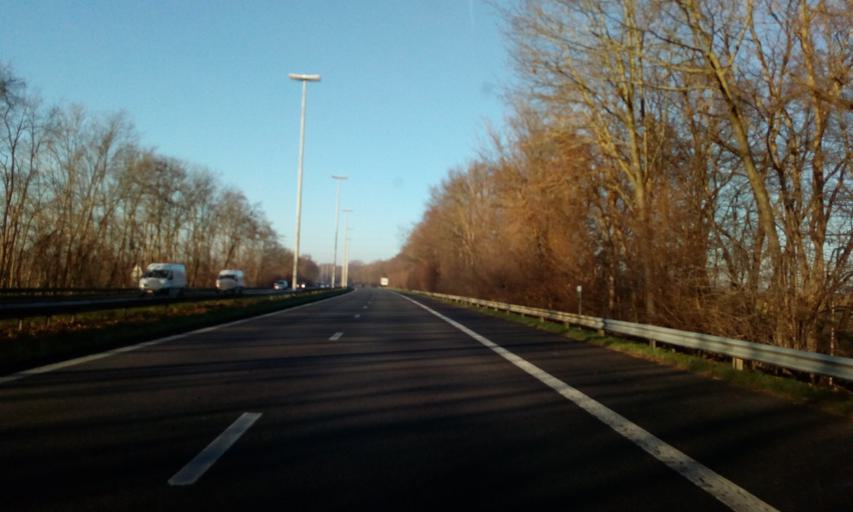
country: BE
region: Wallonia
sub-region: Province du Hainaut
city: Pont-a-Celles
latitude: 50.5468
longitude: 4.3712
